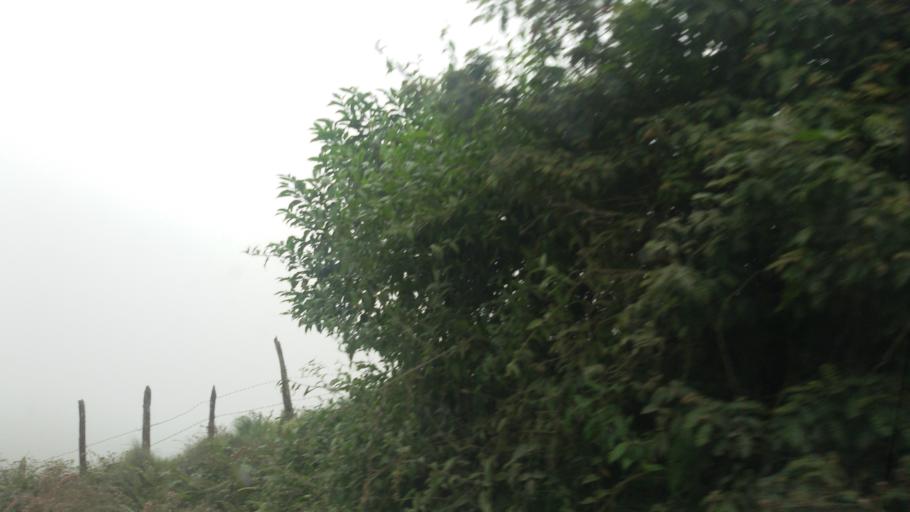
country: CR
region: San Jose
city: Ipis
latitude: 10.0141
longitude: -83.9517
